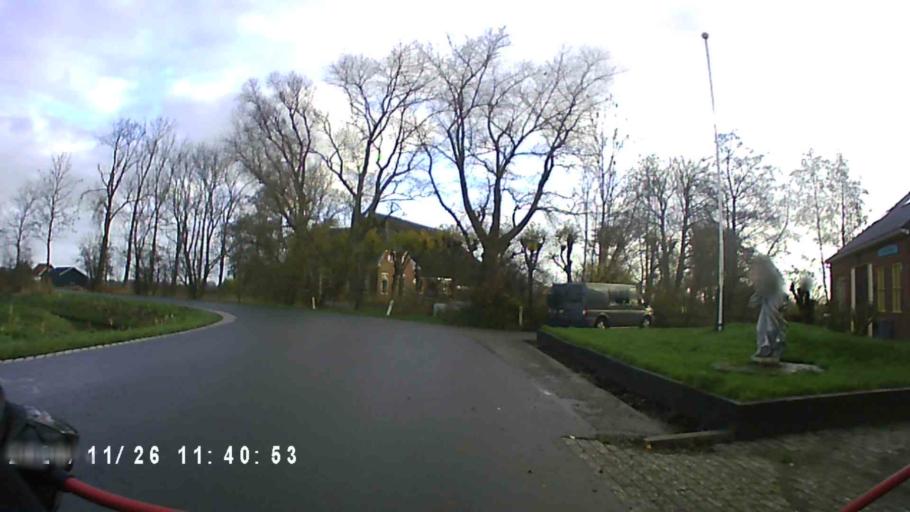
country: NL
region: Groningen
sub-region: Gemeente Bedum
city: Bedum
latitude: 53.2890
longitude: 6.5705
